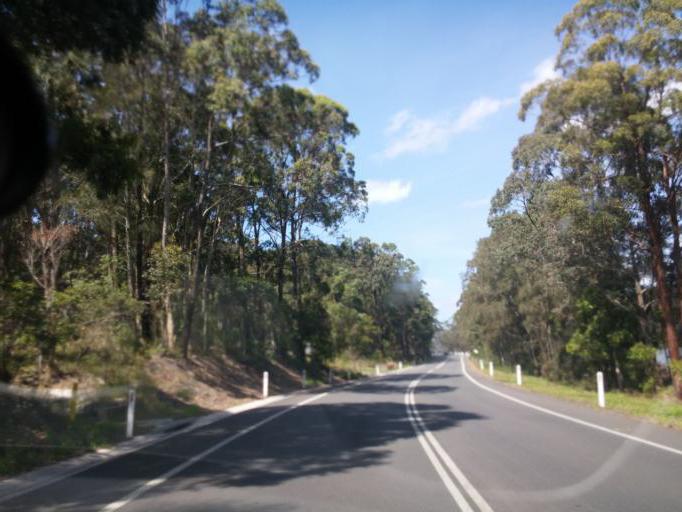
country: AU
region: New South Wales
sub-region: Great Lakes
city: Forster
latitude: -32.3702
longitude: 152.4817
